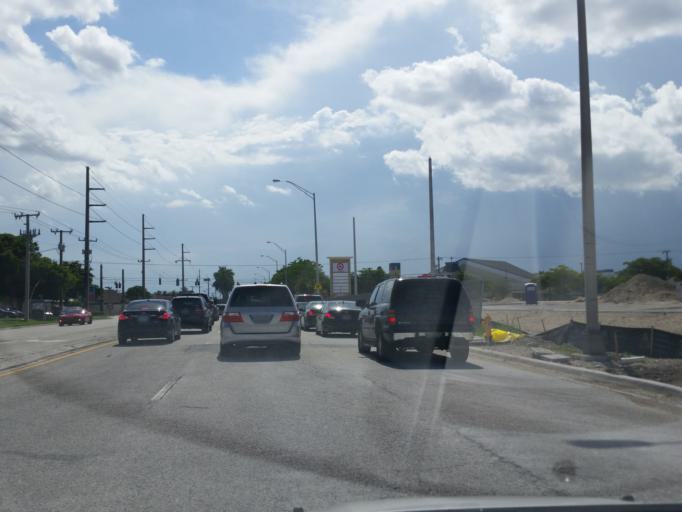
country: US
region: Florida
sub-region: Miami-Dade County
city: Fountainebleau
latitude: 25.7689
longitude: -80.3595
